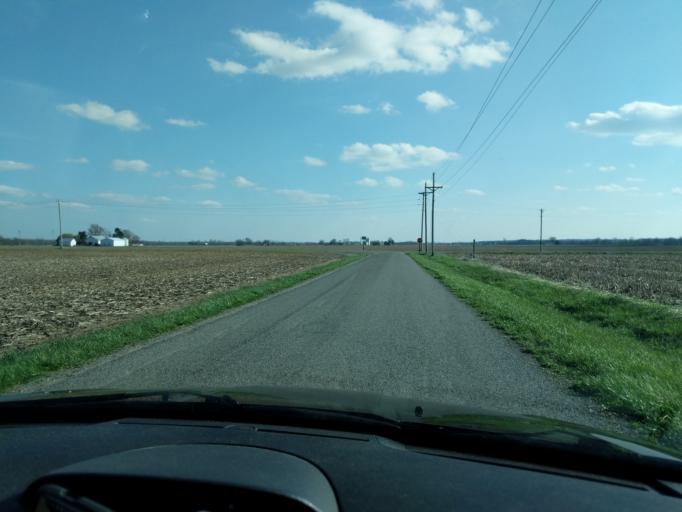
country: US
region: Ohio
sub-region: Champaign County
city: Urbana
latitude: 40.1237
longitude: -83.8115
